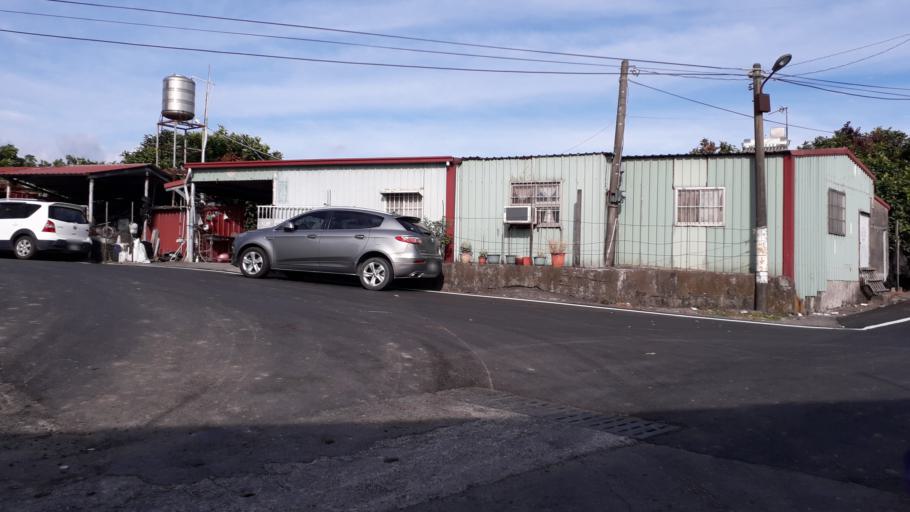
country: TW
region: Taiwan
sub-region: Pingtung
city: Pingtung
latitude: 22.3629
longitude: 120.6034
